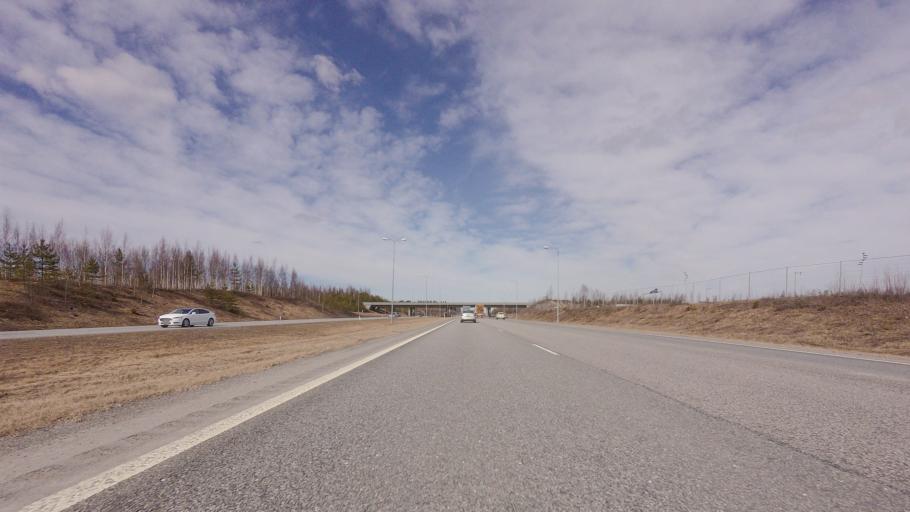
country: FI
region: Pirkanmaa
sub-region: Tampere
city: Lempaeaelae
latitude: 61.3647
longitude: 23.7912
